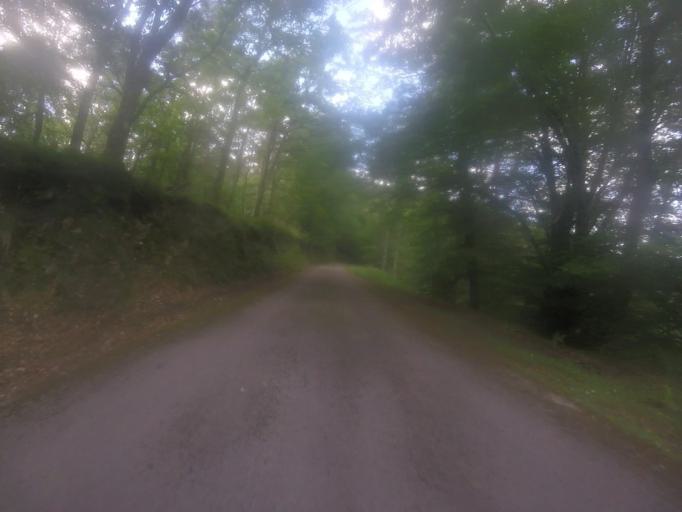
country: ES
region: Navarre
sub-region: Provincia de Navarra
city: Goizueta
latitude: 43.2233
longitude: -1.8023
